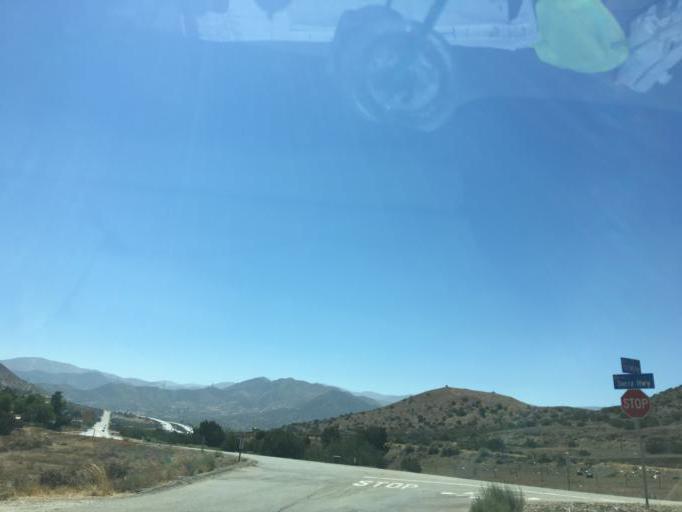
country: US
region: California
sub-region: Los Angeles County
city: Acton
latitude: 34.4944
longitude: -118.1724
